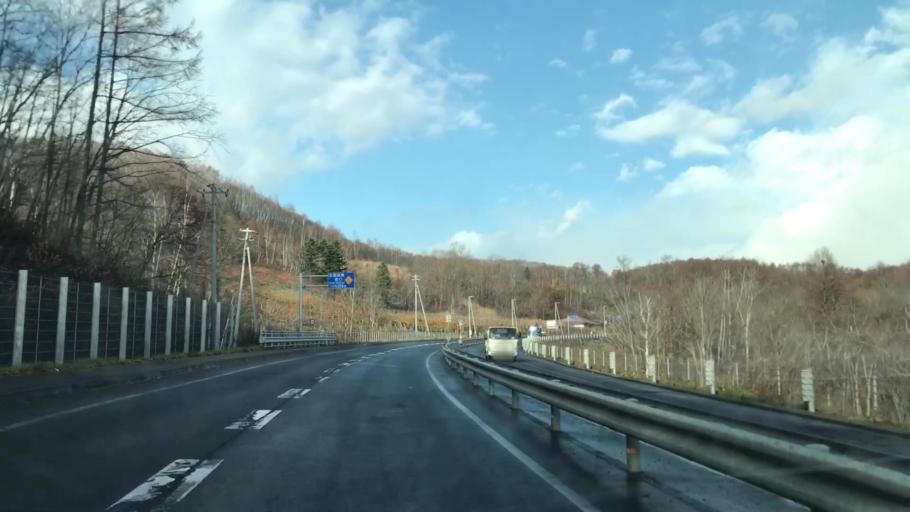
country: JP
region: Hokkaido
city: Yoichi
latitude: 43.2155
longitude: 140.7449
